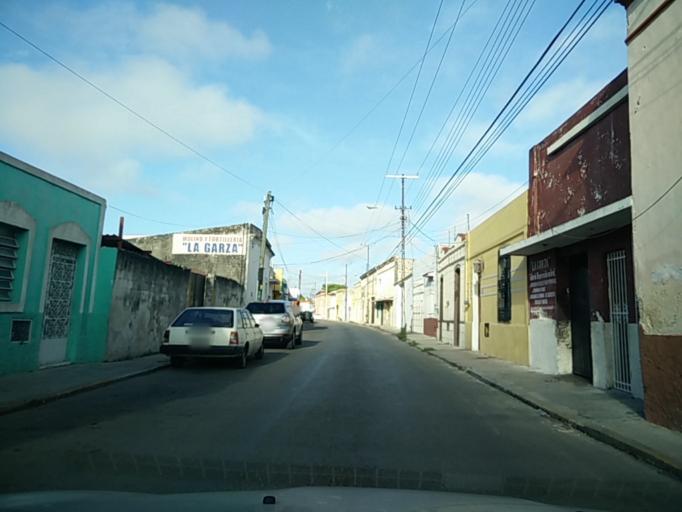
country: MX
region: Yucatan
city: Merida
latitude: 20.9671
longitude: -89.6331
